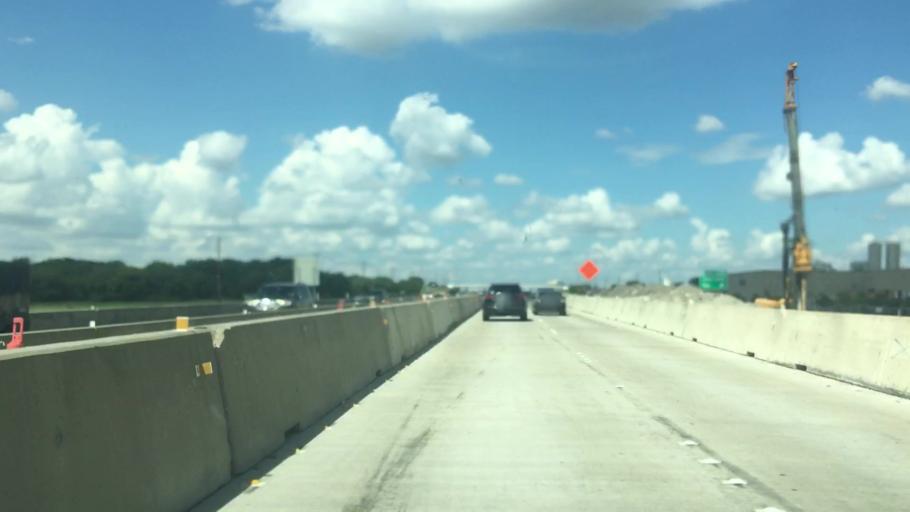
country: US
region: Texas
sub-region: Ellis County
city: Oak Leaf
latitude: 32.4684
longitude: -96.8398
